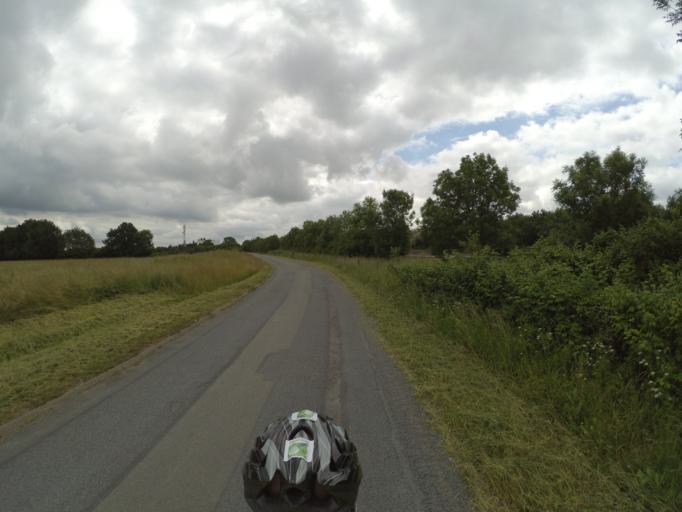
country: FR
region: Poitou-Charentes
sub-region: Departement de la Charente-Maritime
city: Breuil-Magne
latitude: 45.9667
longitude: -0.9753
